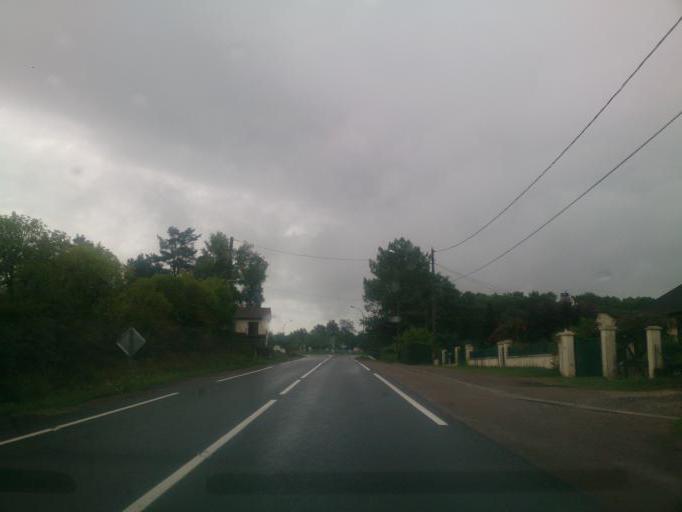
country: FR
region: Limousin
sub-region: Departement de la Correze
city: Malemort-sur-Correze
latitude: 45.1843
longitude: 1.5806
